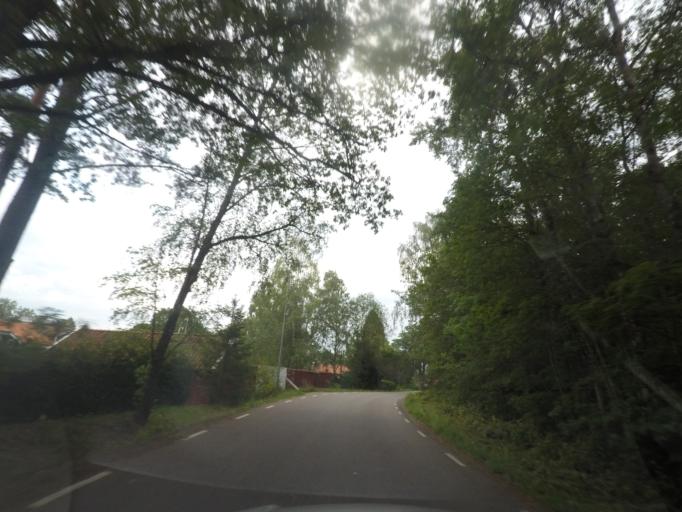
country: SE
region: Vaestmanland
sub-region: Hallstahammars Kommun
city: Kolback
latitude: 59.5281
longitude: 16.2328
